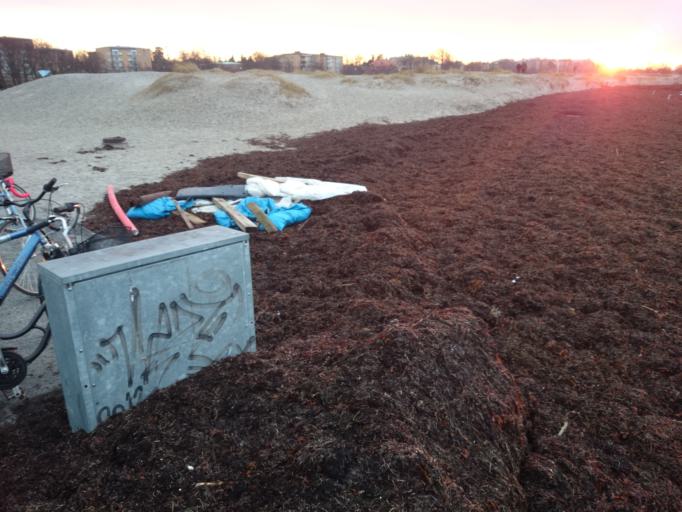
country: SE
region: Skane
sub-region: Malmo
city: Malmoe
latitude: 55.6035
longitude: 12.9670
